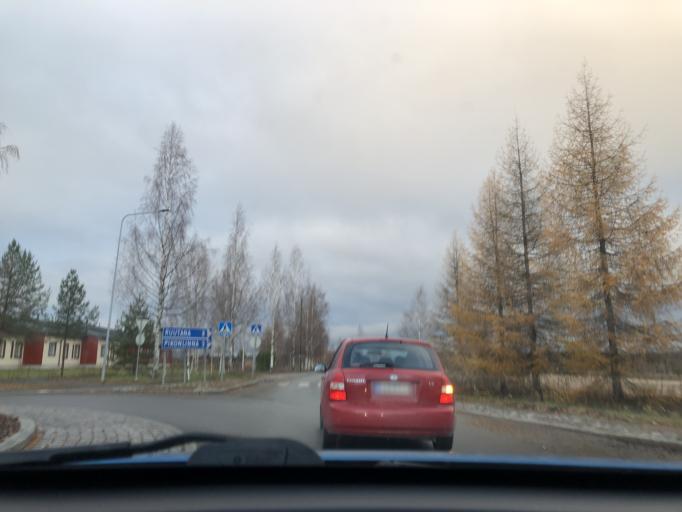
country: FI
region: Pirkanmaa
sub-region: Tampere
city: Kangasala
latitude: 61.4706
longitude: 24.0579
